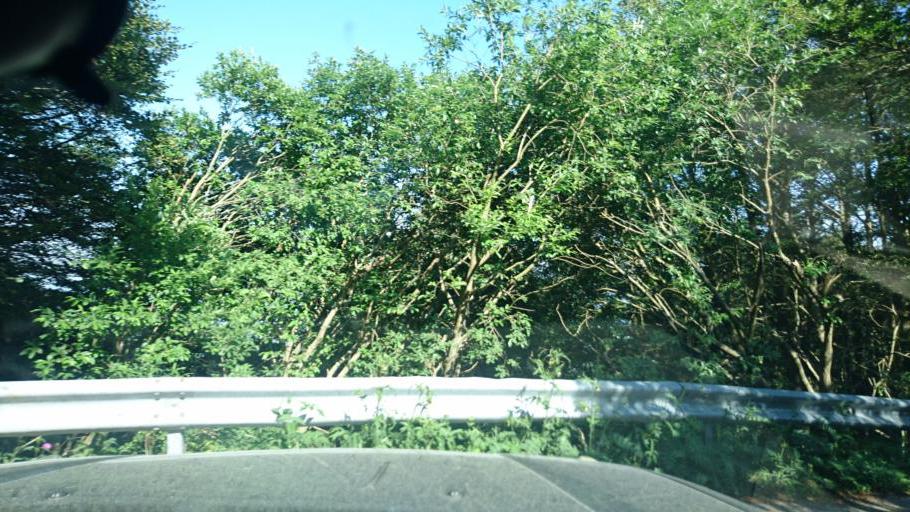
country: IT
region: Veneto
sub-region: Provincia di Treviso
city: Possagno
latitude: 45.8776
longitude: 11.8451
